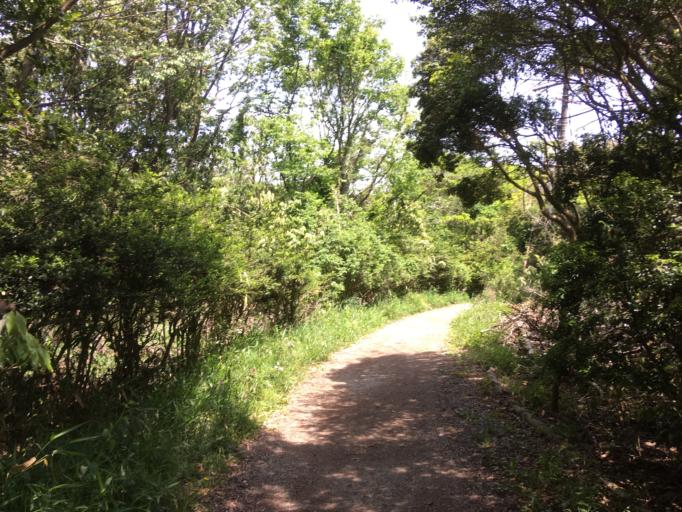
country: JP
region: Nara
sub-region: Ikoma-shi
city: Ikoma
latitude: 34.6624
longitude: 135.6698
